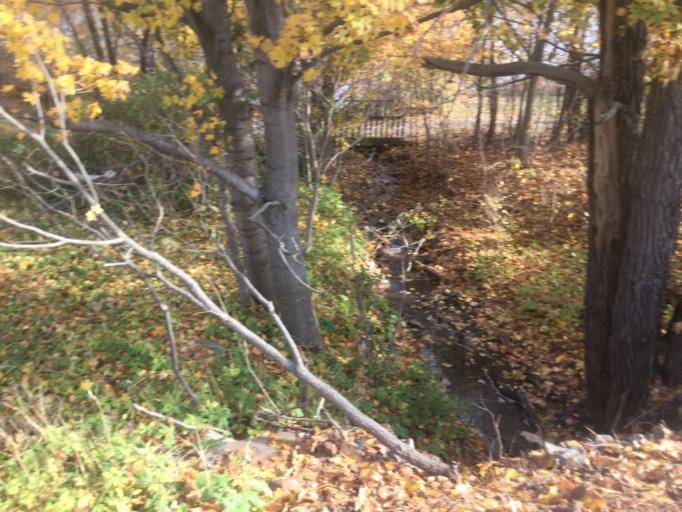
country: CA
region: Nova Scotia
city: New Glasgow
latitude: 45.5827
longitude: -62.6543
